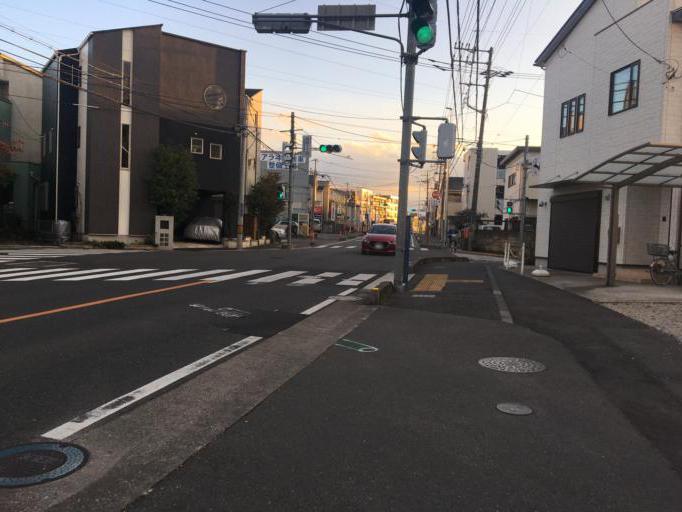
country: JP
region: Saitama
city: Shiki
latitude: 35.8322
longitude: 139.5756
